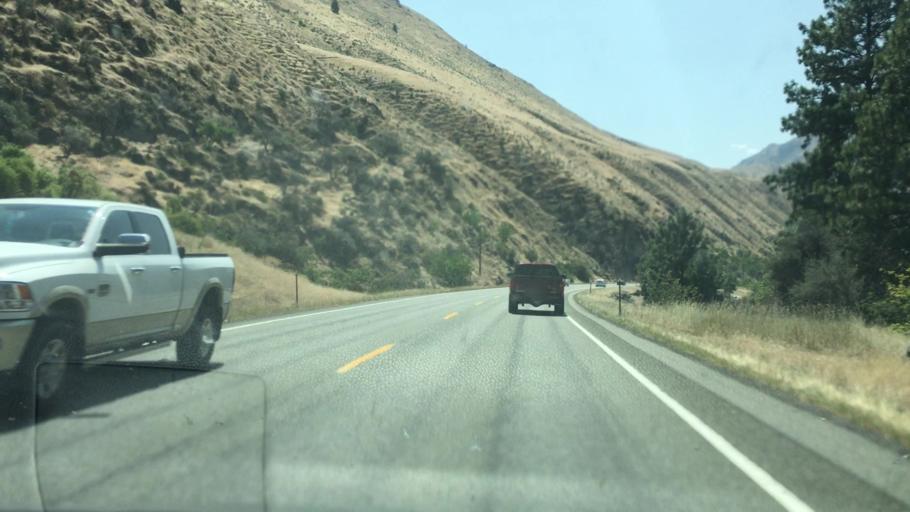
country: US
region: Idaho
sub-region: Idaho County
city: Grangeville
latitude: 45.5032
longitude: -116.2961
